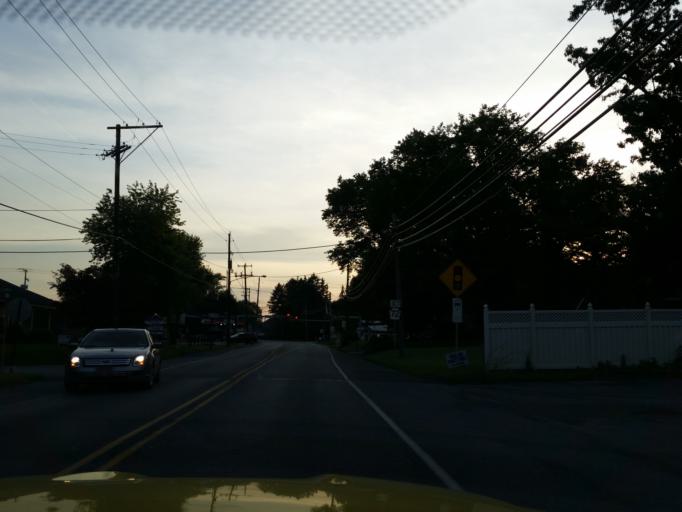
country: US
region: Pennsylvania
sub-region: Lebanon County
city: Jonestown
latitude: 40.4125
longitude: -76.4951
